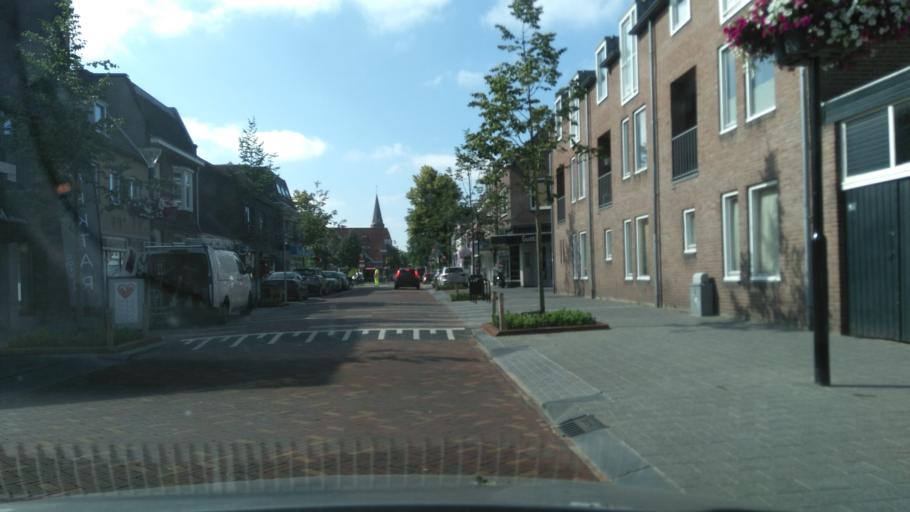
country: NL
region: North Brabant
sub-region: Gemeente Goirle
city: Goirle
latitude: 51.5218
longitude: 5.0667
